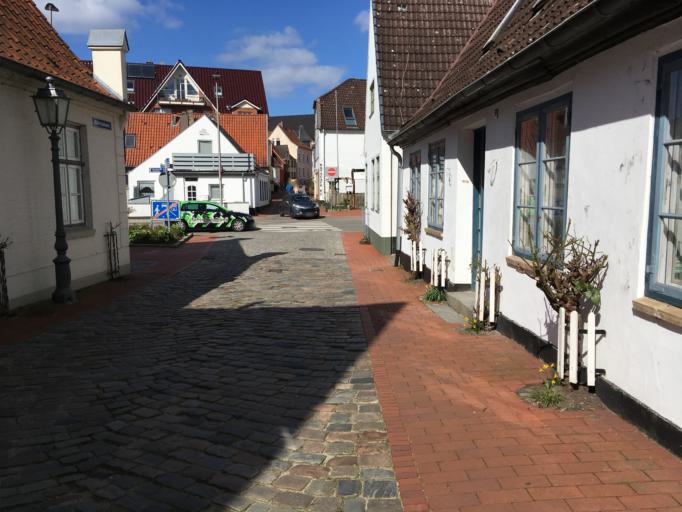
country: DE
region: Schleswig-Holstein
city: Schleswig
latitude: 54.5130
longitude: 9.5737
